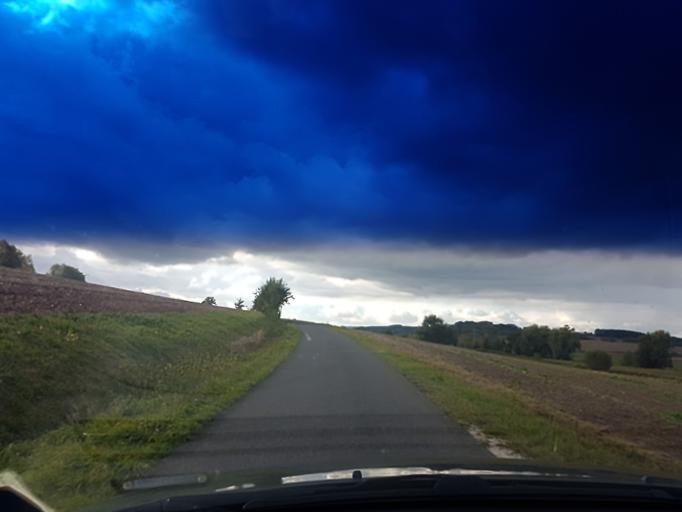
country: DE
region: Bavaria
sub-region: Upper Franconia
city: Schlusselfeld
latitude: 49.7612
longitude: 10.5966
